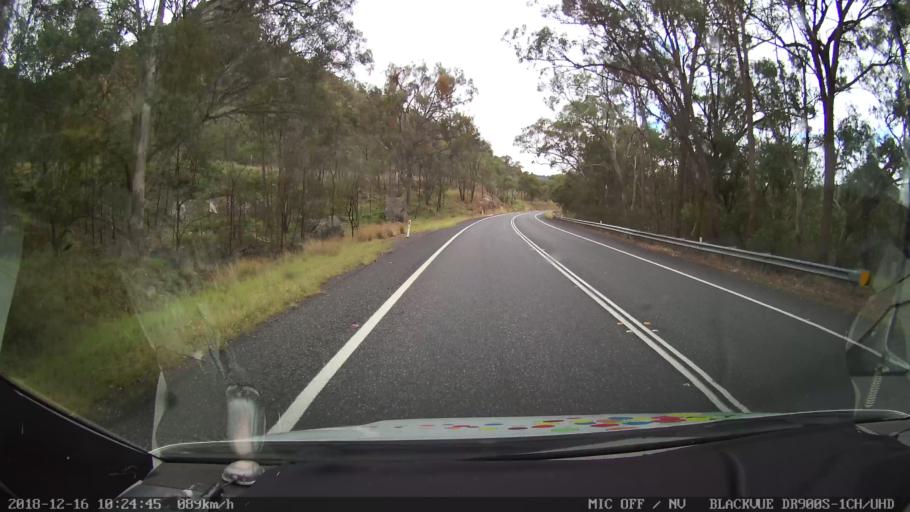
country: AU
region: New South Wales
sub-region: Tenterfield Municipality
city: Carrolls Creek
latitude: -29.1673
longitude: 152.0037
